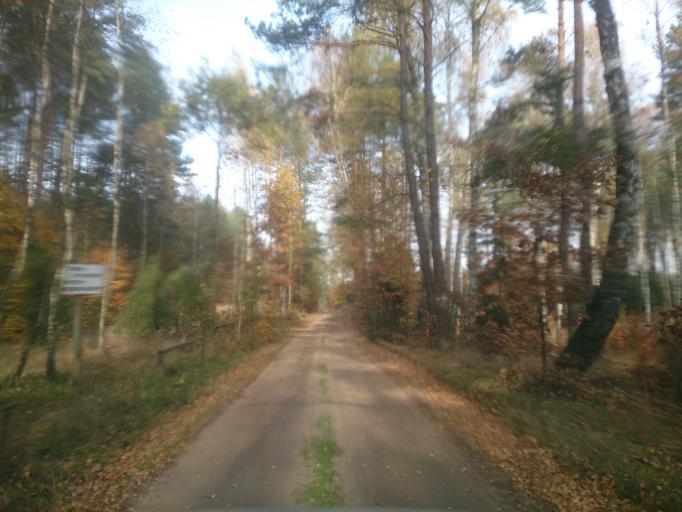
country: PL
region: Kujawsko-Pomorskie
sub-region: Powiat brodnicki
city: Bobrowo
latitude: 53.3654
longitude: 19.3456
